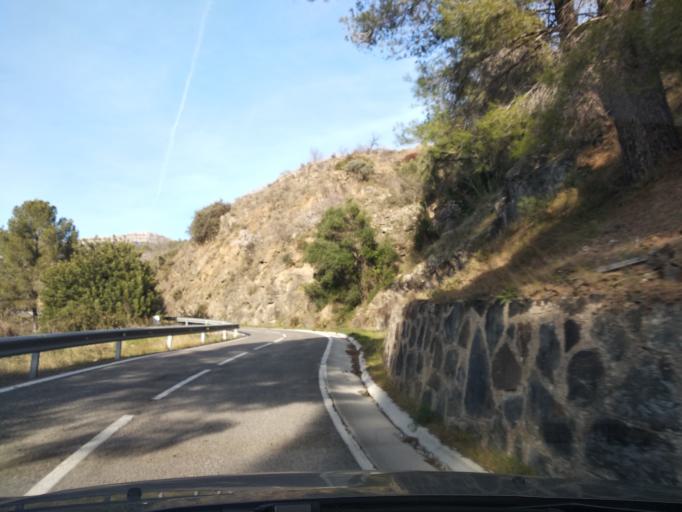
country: ES
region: Catalonia
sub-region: Provincia de Tarragona
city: Margalef
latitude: 41.2320
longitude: 0.7810
